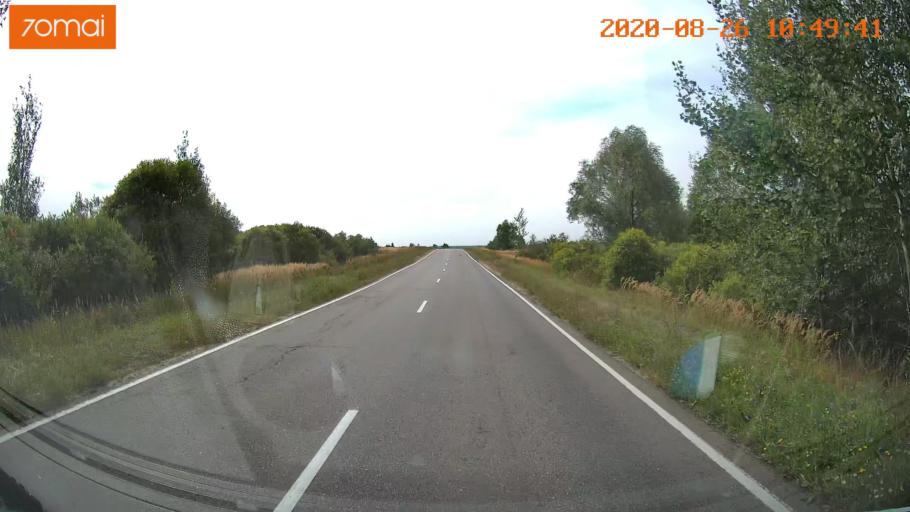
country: RU
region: Rjazan
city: Lashma
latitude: 54.6988
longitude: 41.1584
